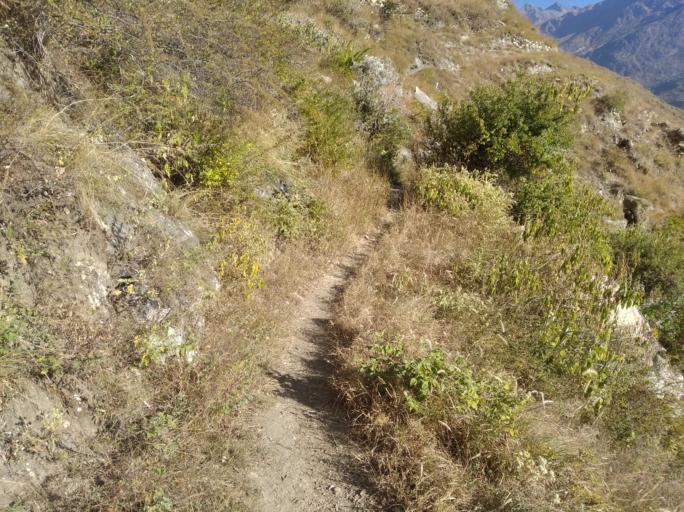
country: NP
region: Western Region
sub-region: Dhawalagiri Zone
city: Jomsom
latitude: 28.8823
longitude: 82.9691
